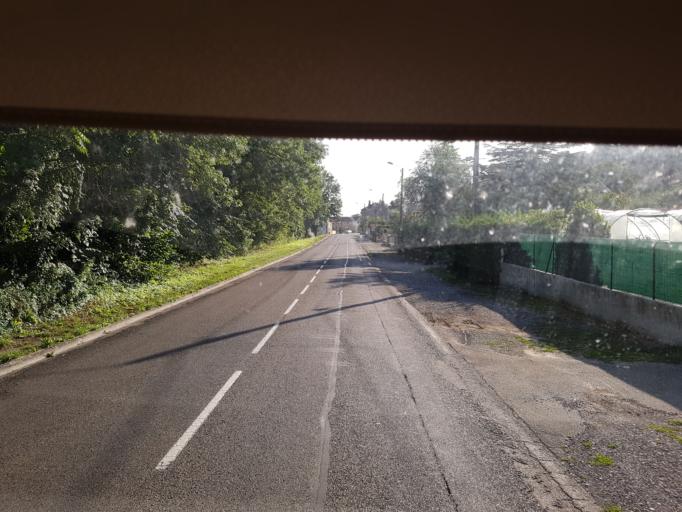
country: FR
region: Rhone-Alpes
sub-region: Departement de l'Ain
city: Neuville-sur-Ain
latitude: 46.0564
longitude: 5.3648
